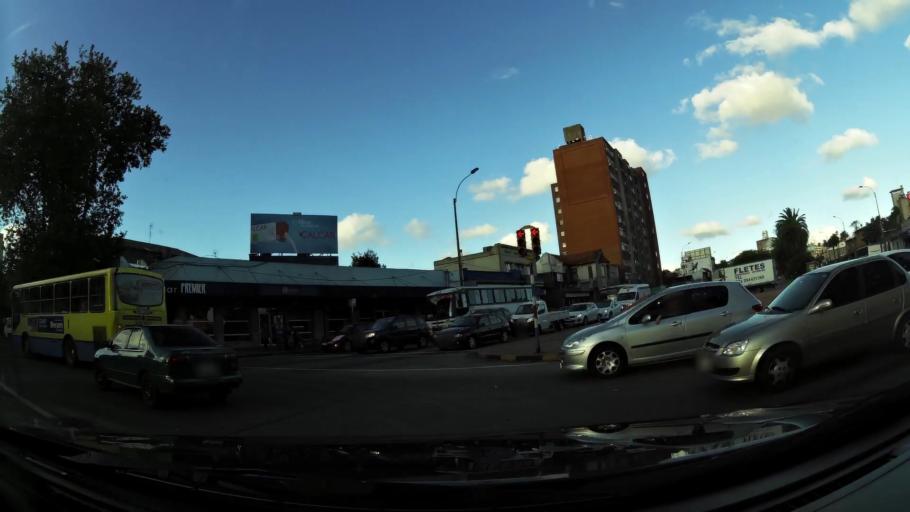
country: UY
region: Montevideo
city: Montevideo
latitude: -34.8876
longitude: -56.1447
